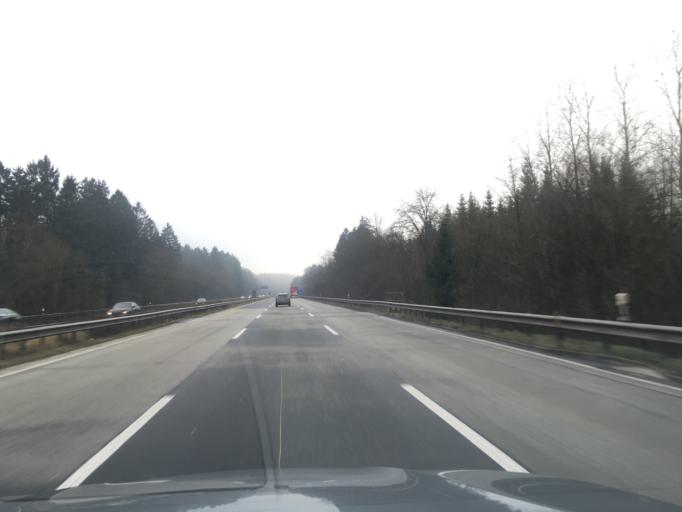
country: DE
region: Rheinland-Pfalz
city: Ebernhahn
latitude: 50.4554
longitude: 7.7480
